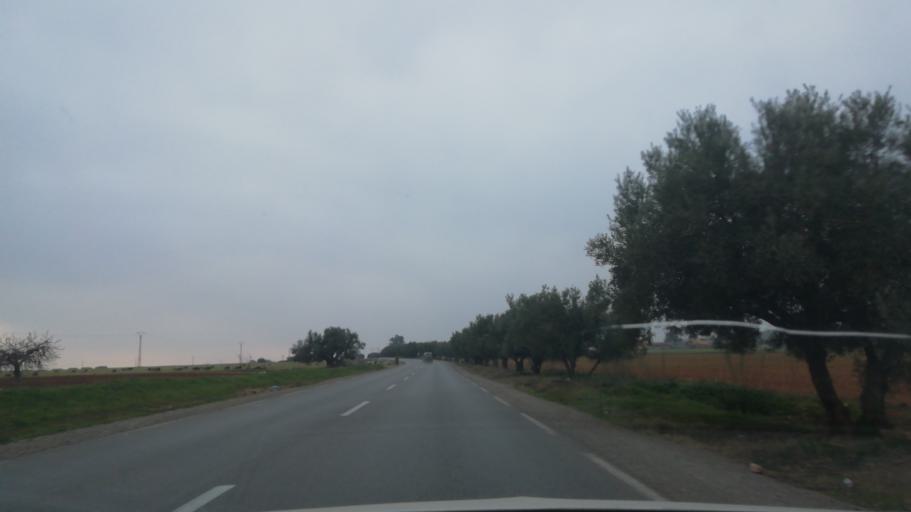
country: DZ
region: Sidi Bel Abbes
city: Sfizef
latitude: 35.2564
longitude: -0.1861
